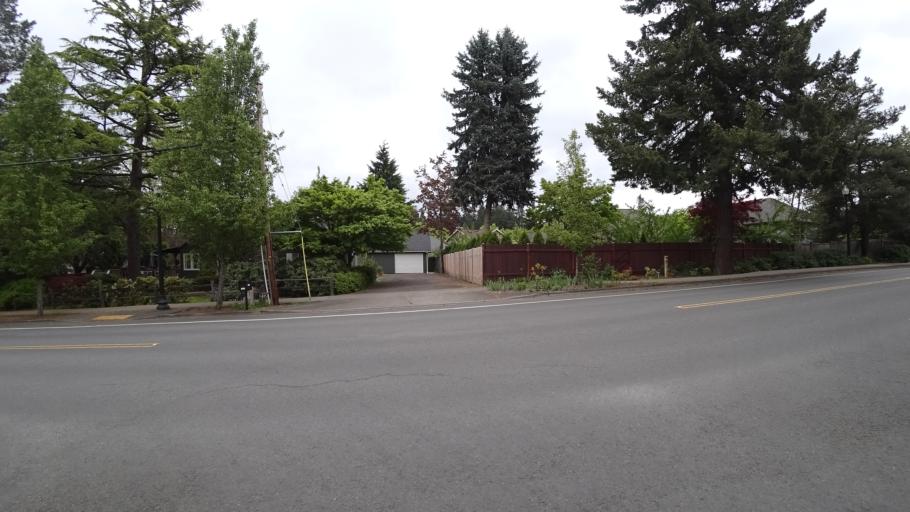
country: US
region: Oregon
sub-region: Washington County
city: Beaverton
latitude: 45.4628
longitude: -122.8364
